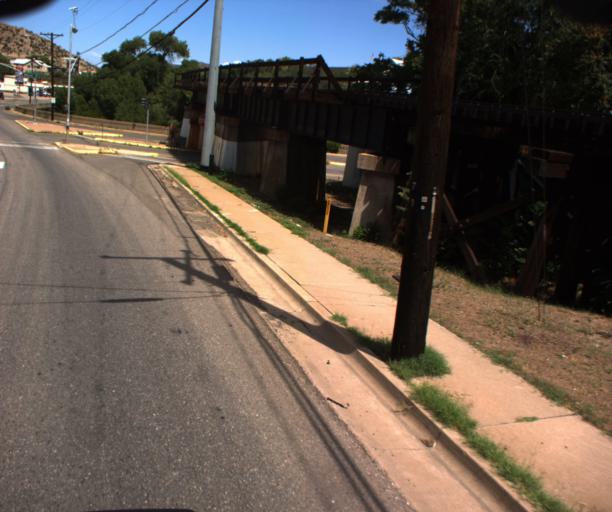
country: US
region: Arizona
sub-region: Gila County
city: Globe
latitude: 33.4011
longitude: -110.7916
